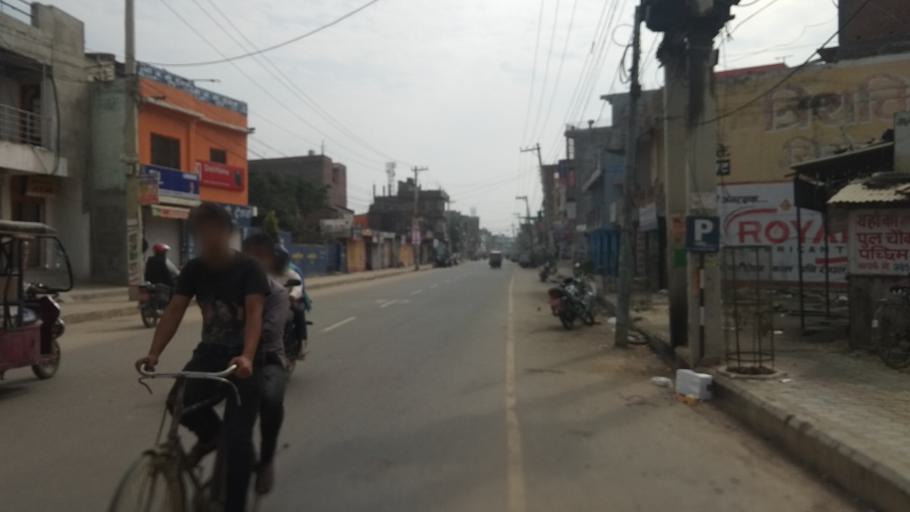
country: NP
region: Central Region
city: Janakpur
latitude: 26.7348
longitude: 85.9323
